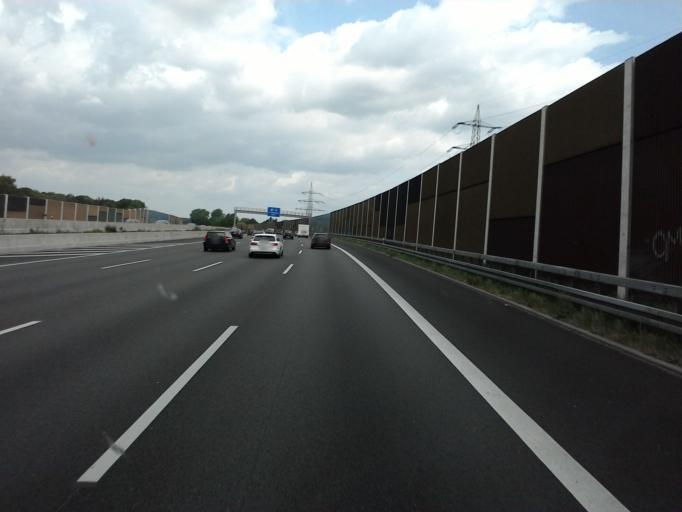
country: DE
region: North Rhine-Westphalia
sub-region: Regierungsbezirk Koln
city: Buchheim
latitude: 50.9743
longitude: 7.0285
